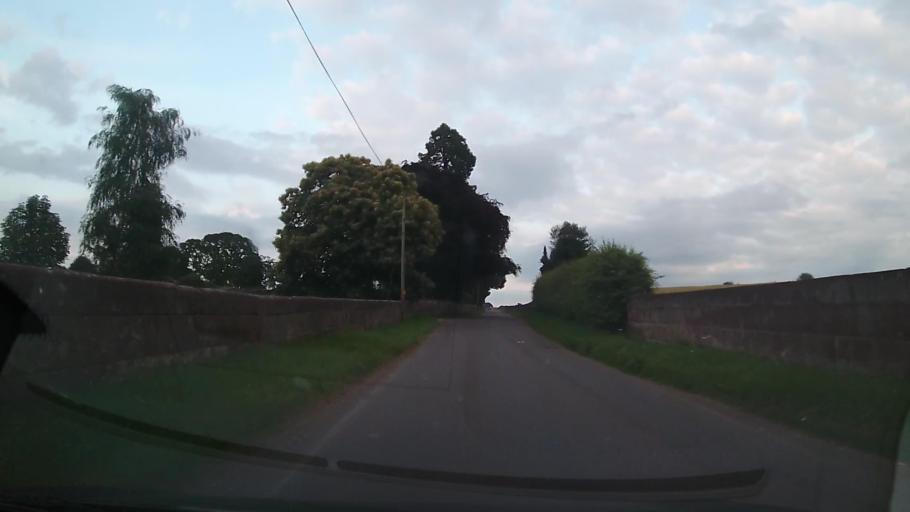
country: GB
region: England
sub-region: Shropshire
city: Clive
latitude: 52.8101
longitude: -2.7713
